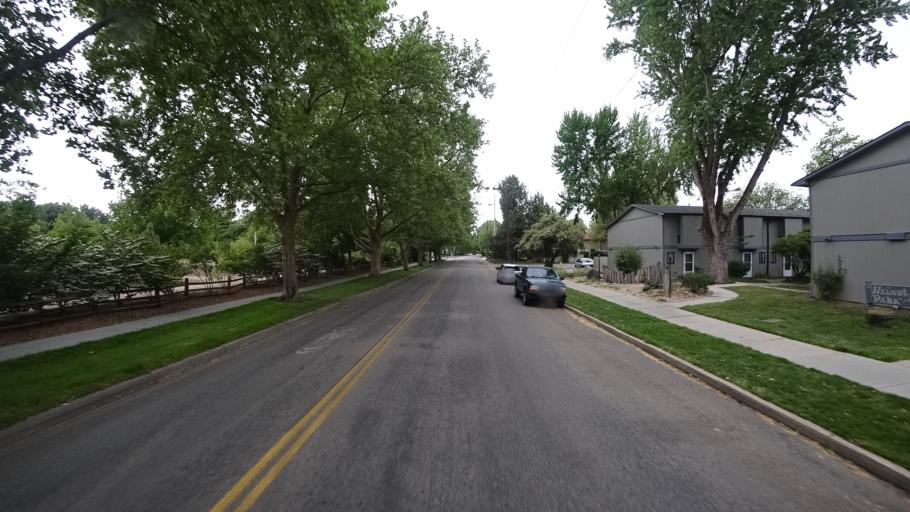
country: US
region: Idaho
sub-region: Ada County
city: Boise
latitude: 43.6053
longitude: -116.1841
